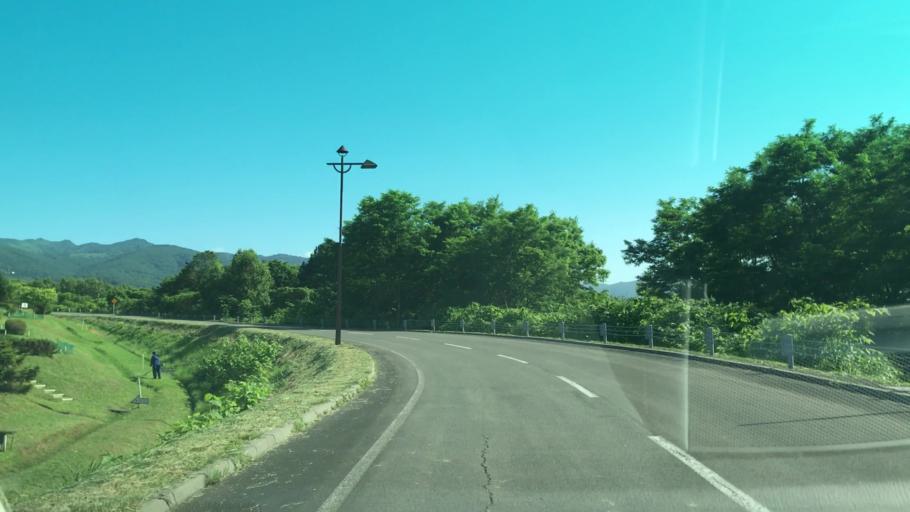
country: JP
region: Hokkaido
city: Iwanai
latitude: 42.9763
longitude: 140.6080
